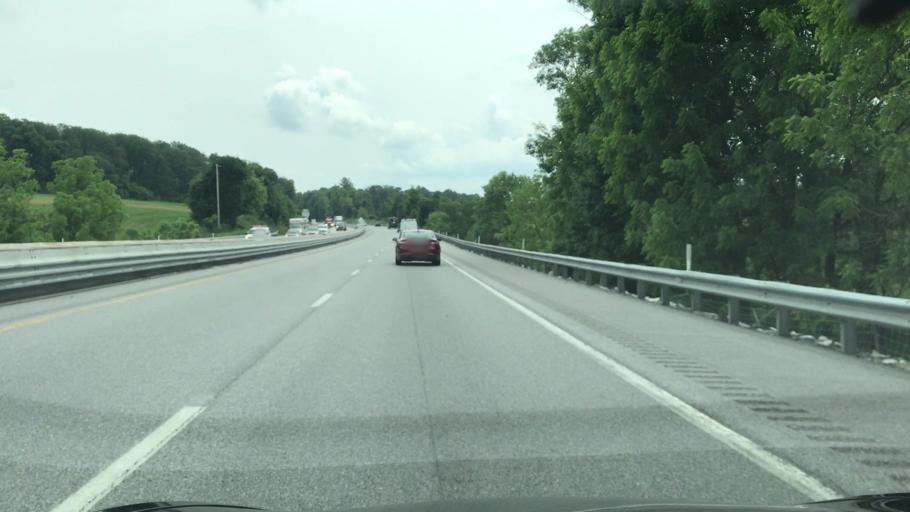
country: US
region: Pennsylvania
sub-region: York County
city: Shrewsbury
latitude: 39.7323
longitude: -76.6598
